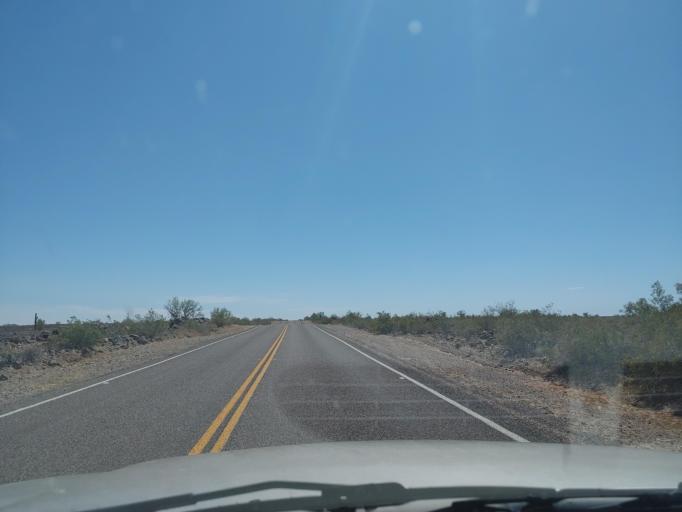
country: US
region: Arizona
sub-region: Maricopa County
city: Gila Bend
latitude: 32.9057
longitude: -113.2638
